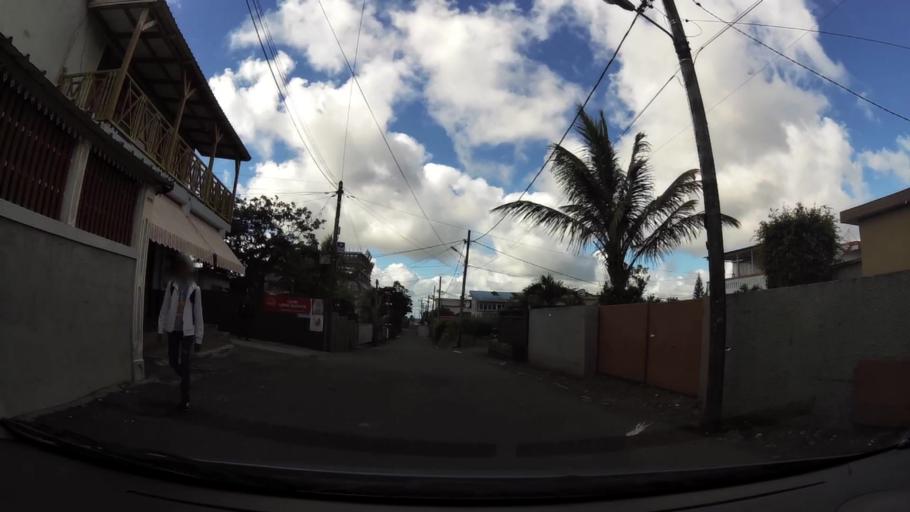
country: MU
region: Plaines Wilhems
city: Curepipe
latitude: -20.3237
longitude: 57.5352
